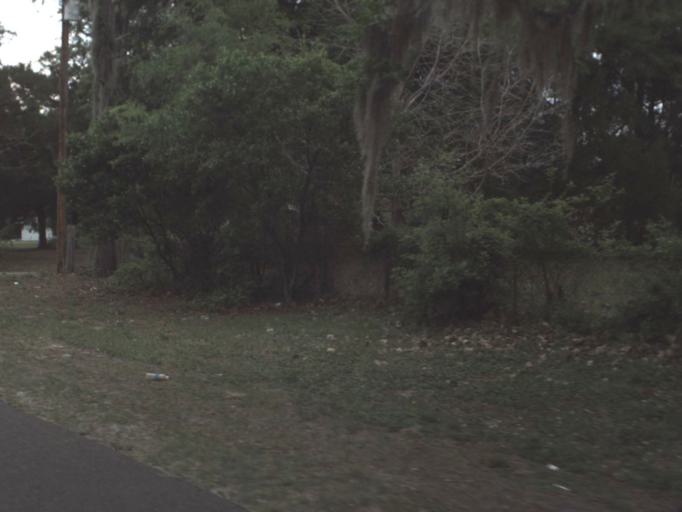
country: US
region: Florida
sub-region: Lake County
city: Umatilla
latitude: 28.9825
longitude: -81.6445
